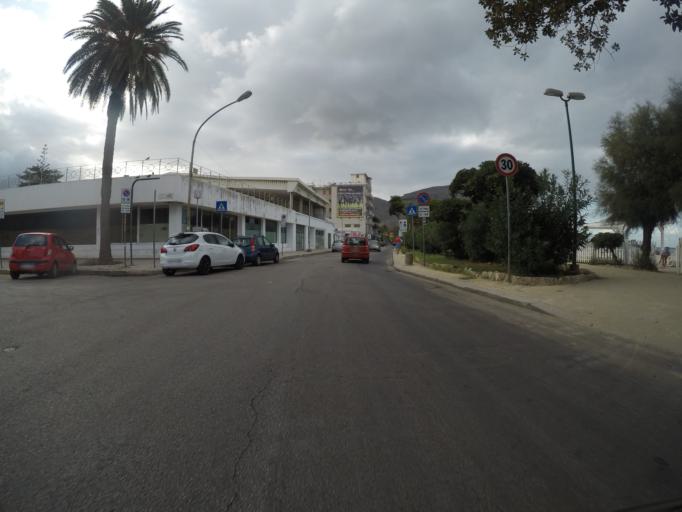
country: IT
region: Sicily
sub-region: Palermo
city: Palermo
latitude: 38.1973
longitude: 13.3314
